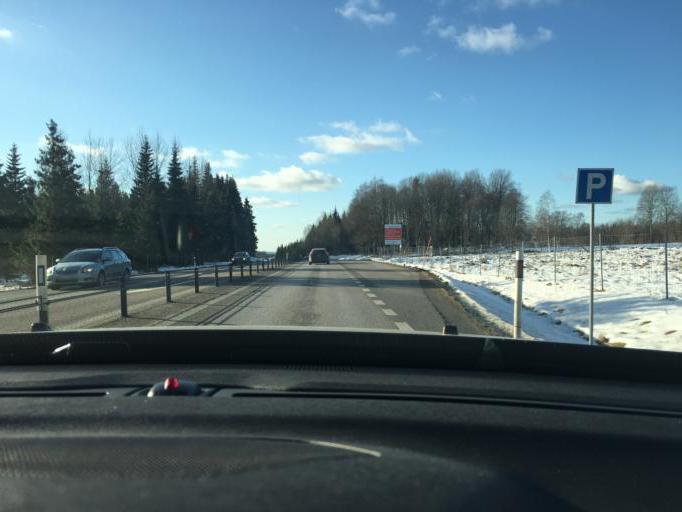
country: SE
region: Vaestra Goetaland
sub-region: Ulricehamns Kommun
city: Ulricehamn
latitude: 57.8021
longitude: 13.4989
